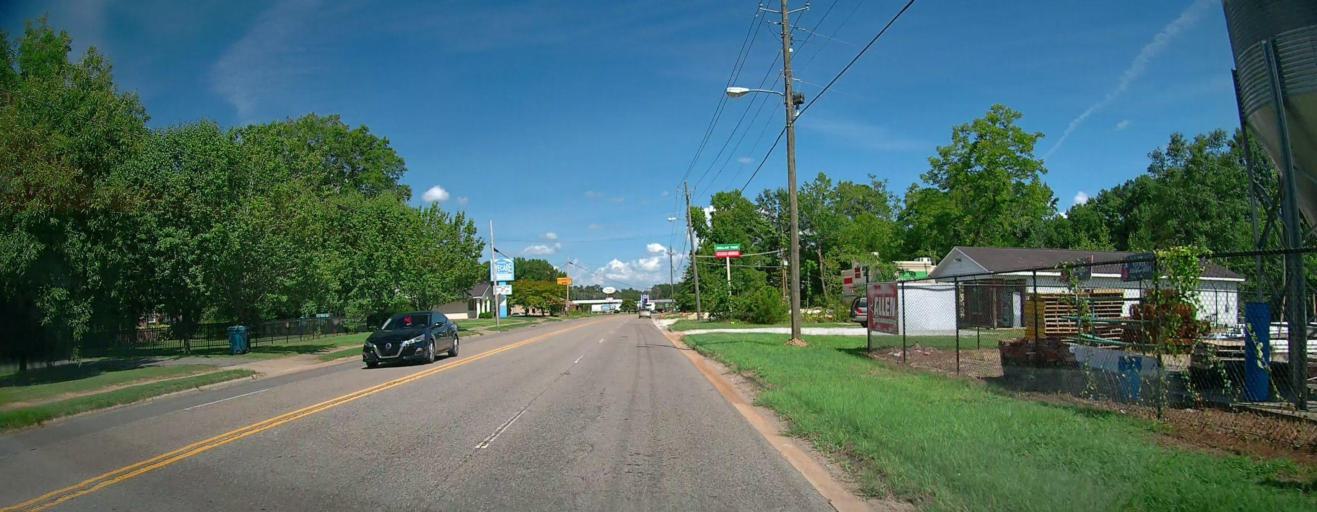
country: US
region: Alabama
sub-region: Pickens County
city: Reform
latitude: 33.3783
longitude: -88.0139
